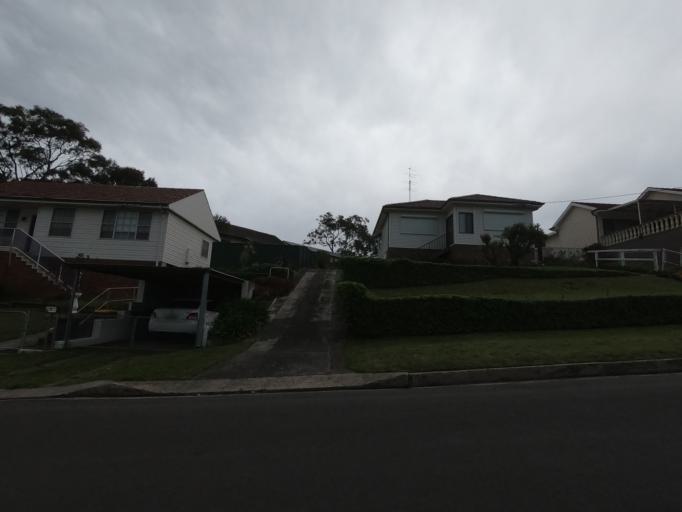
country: AU
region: New South Wales
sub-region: Wollongong
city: Lake Heights
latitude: -34.4839
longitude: 150.8648
